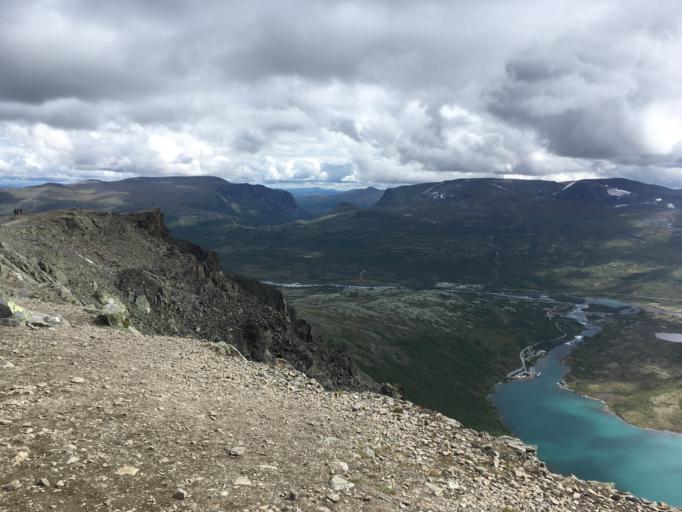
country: NO
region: Oppland
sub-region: Lom
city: Fossbergom
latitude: 61.5069
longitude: 8.7736
